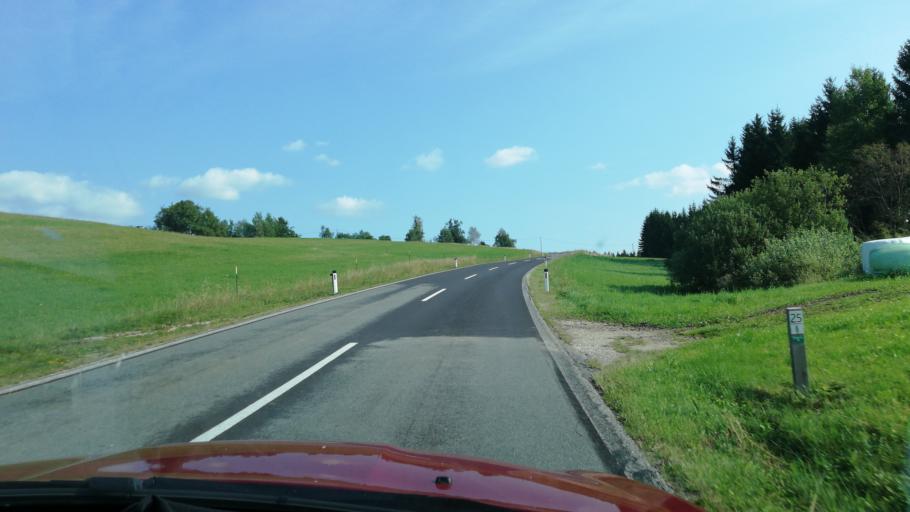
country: AT
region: Lower Austria
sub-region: Politischer Bezirk Zwettl
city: Langschlag
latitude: 48.5087
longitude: 14.8331
